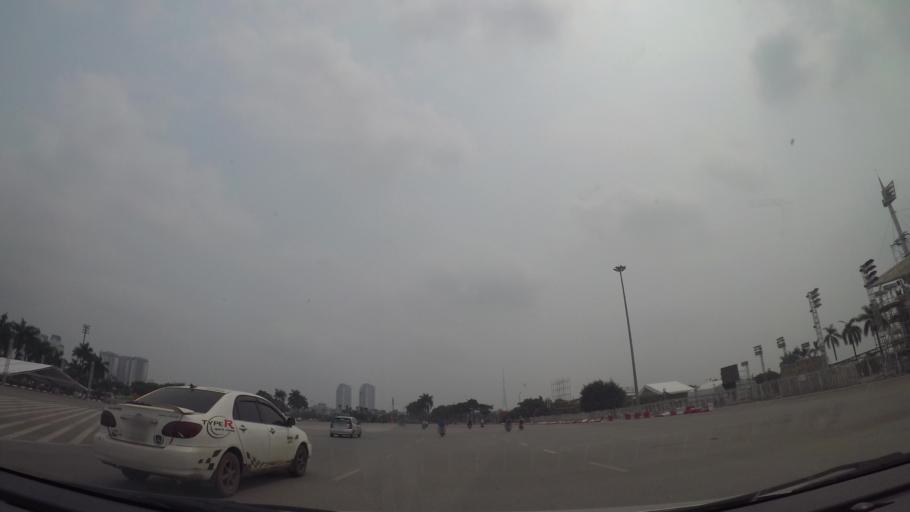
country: VN
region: Ha Noi
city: Cau Dien
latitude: 21.0204
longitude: 105.7661
